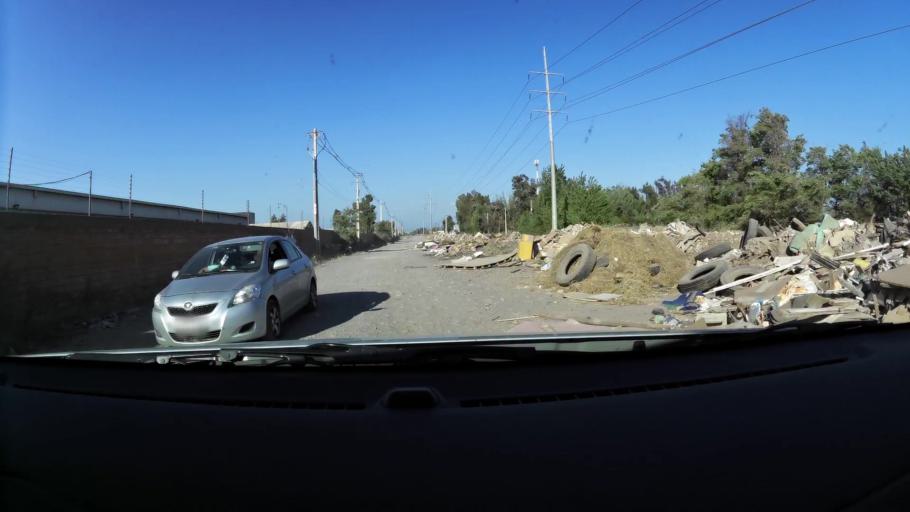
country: CL
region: Santiago Metropolitan
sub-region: Provincia de Maipo
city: San Bernardo
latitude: -33.5346
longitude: -70.7566
